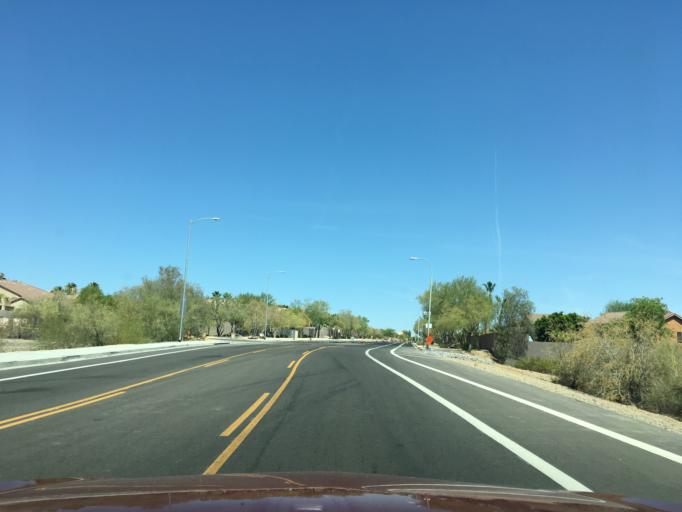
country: US
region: Arizona
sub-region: Maricopa County
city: Laveen
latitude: 33.3030
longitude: -112.1011
